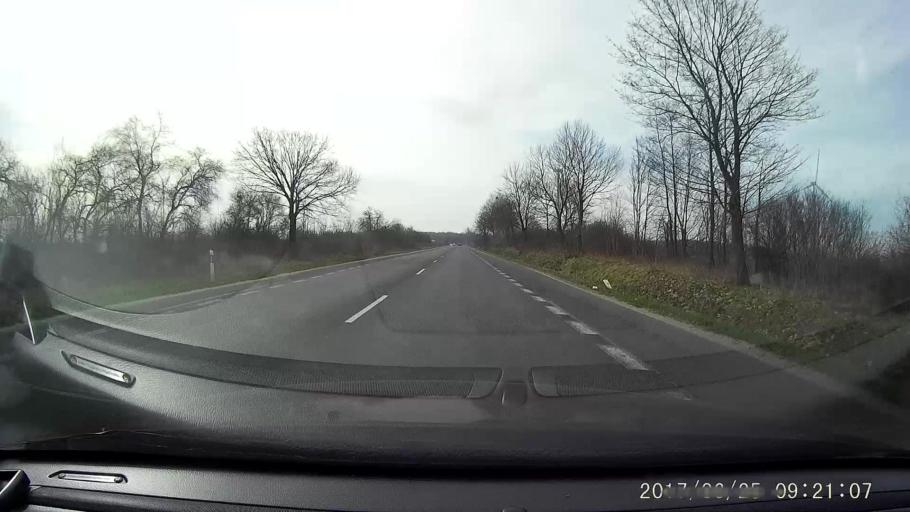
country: PL
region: Lower Silesian Voivodeship
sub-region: Powiat zgorzelecki
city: Sulikow
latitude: 51.0891
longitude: 15.0230
